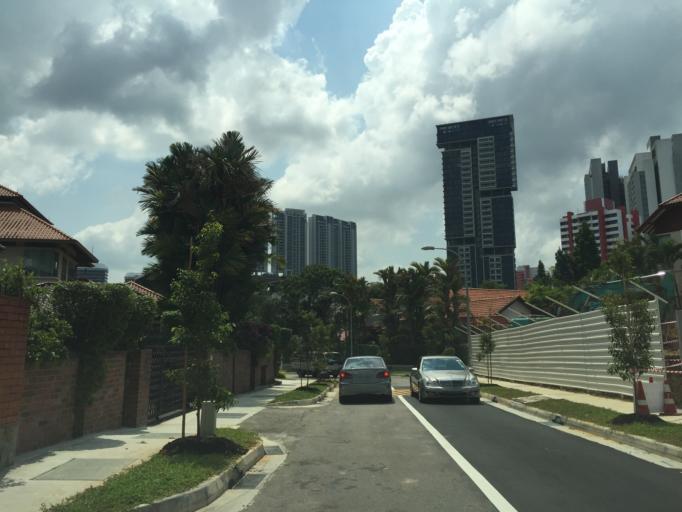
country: SG
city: Singapore
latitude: 1.3257
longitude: 103.8399
